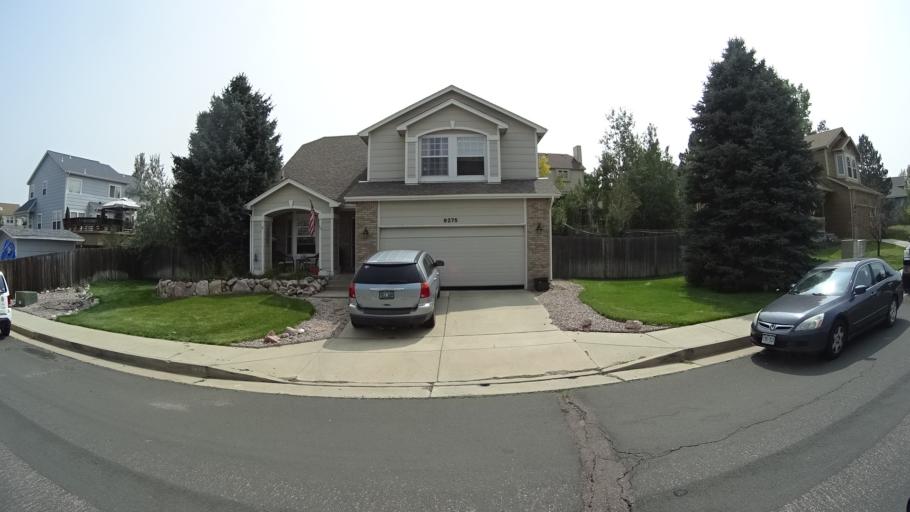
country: US
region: Colorado
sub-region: El Paso County
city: Cimarron Hills
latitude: 38.9206
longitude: -104.7475
